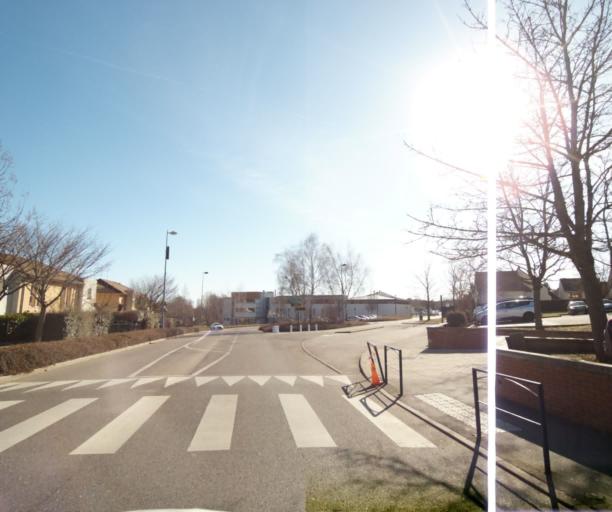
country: FR
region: Lorraine
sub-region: Departement de Meurthe-et-Moselle
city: Ludres
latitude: 48.6200
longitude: 6.1695
